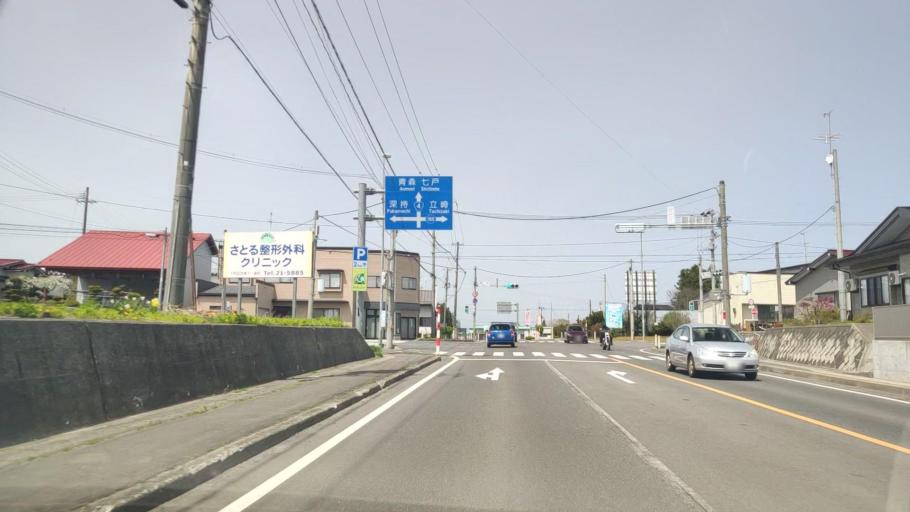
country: JP
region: Aomori
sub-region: Misawa Shi
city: Inuotose
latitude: 40.6580
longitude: 141.1922
